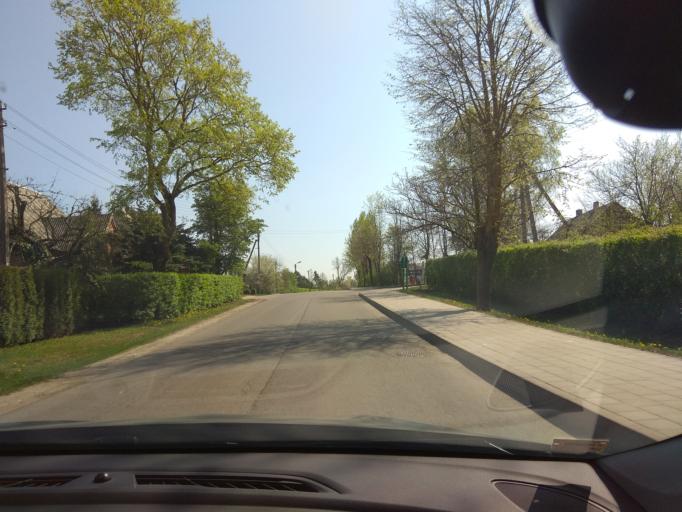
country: LT
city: Linkuva
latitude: 56.0849
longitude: 23.9648
